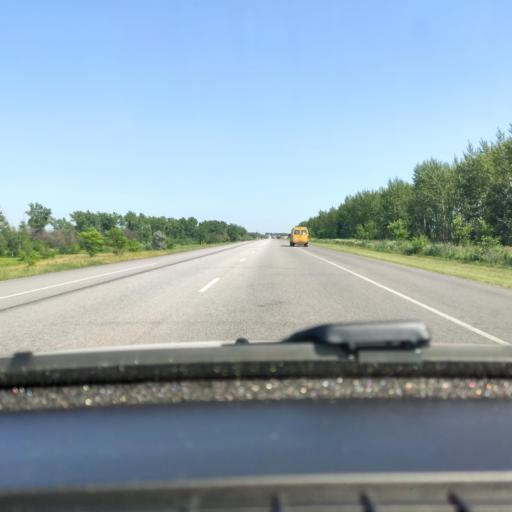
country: RU
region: Voronezj
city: Novaya Usman'
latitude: 51.6924
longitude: 39.4513
